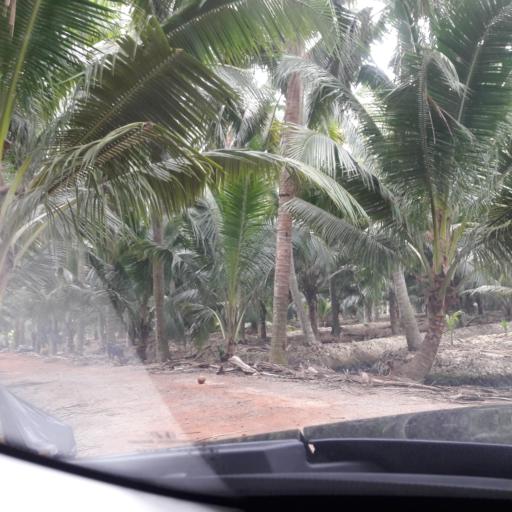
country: TH
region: Ratchaburi
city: Damnoen Saduak
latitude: 13.5705
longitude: 99.9471
